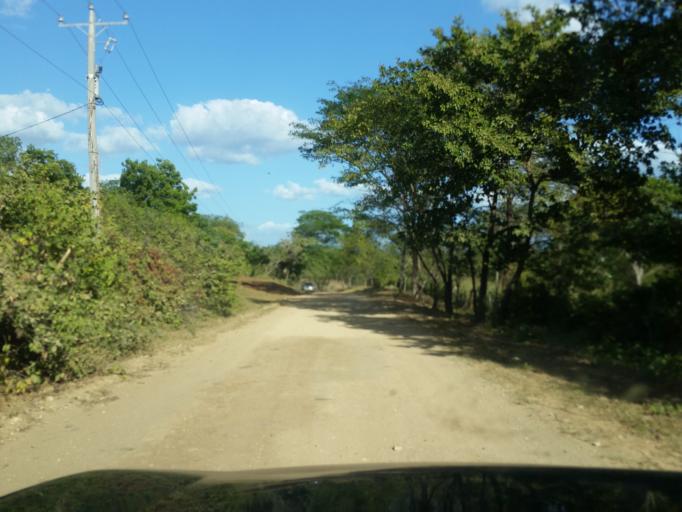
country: NI
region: Managua
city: Carlos Fonseca Amador
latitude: 11.9228
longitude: -86.5917
